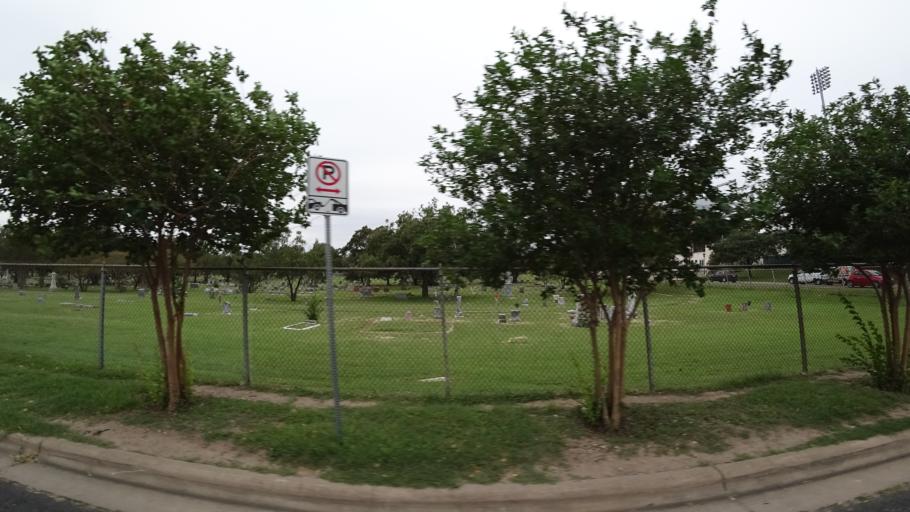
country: US
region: Texas
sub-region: Travis County
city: Austin
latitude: 30.2786
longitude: -97.7251
